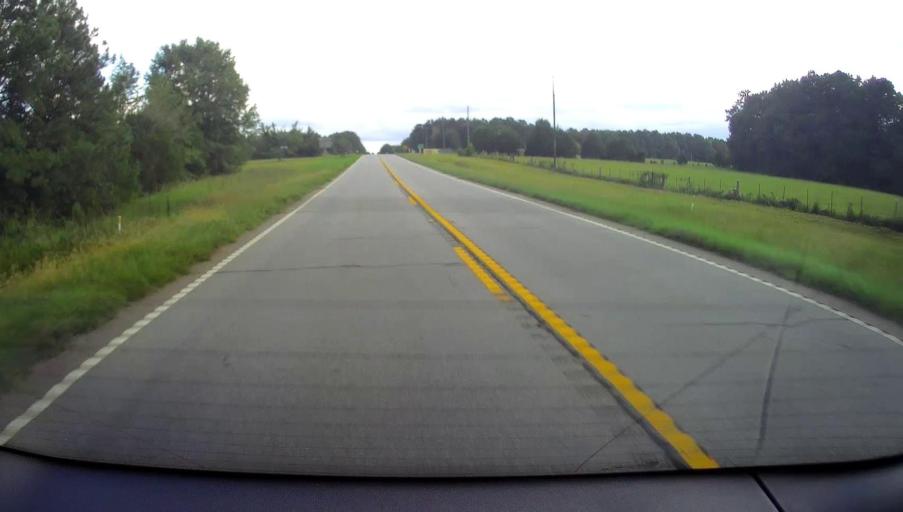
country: US
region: Georgia
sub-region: Meriwether County
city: Greenville
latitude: 33.0389
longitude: -84.5652
